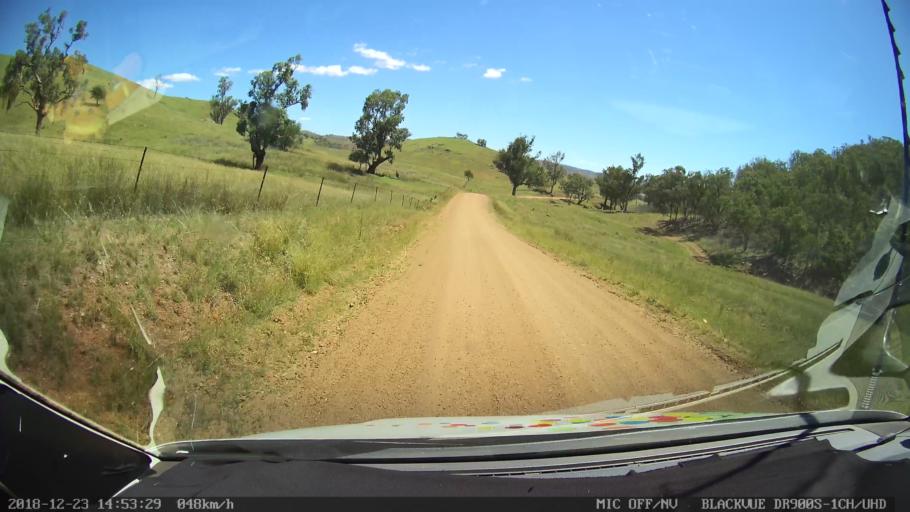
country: AU
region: New South Wales
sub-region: Tamworth Municipality
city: Manilla
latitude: -30.6915
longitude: 150.8515
